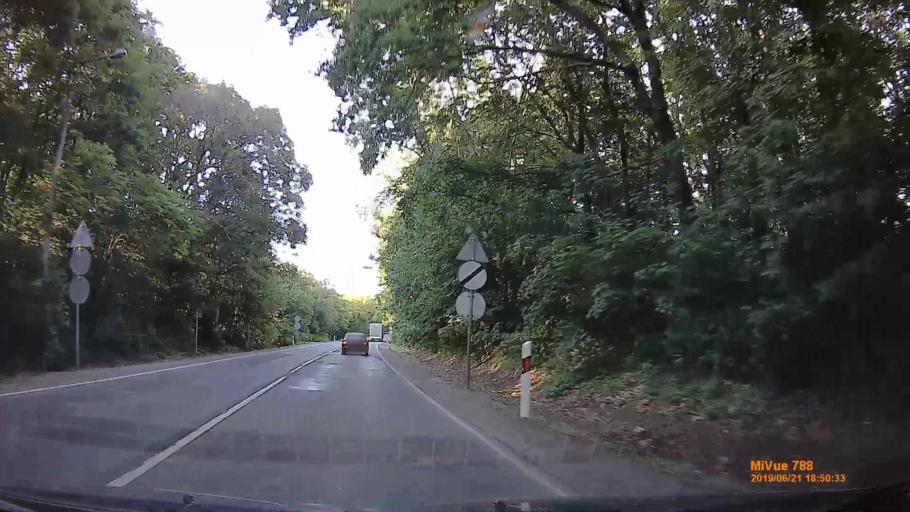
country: HU
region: Fejer
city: dunaujvaros
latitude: 46.9825
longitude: 18.9133
